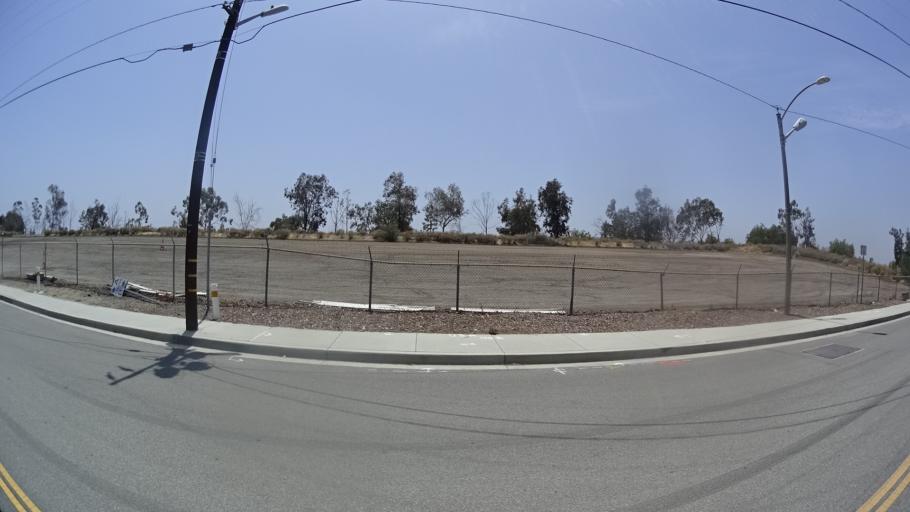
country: US
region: California
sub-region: Los Angeles County
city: Burbank
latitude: 34.2054
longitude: -118.3098
